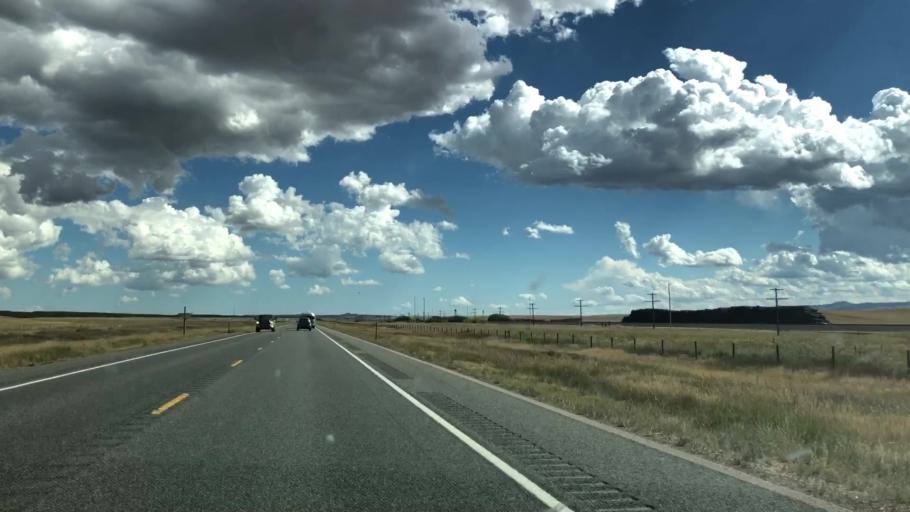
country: US
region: Wyoming
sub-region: Albany County
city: Laramie
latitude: 41.1695
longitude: -105.5852
